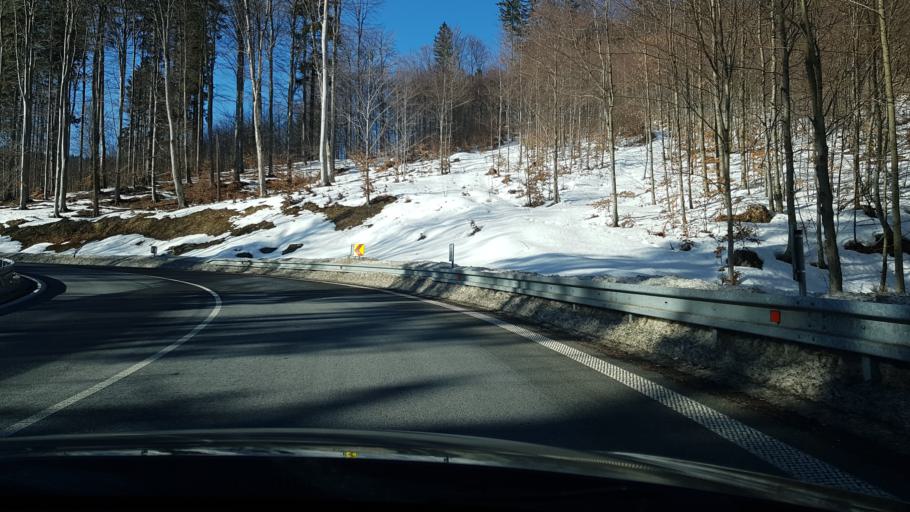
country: CZ
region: Olomoucky
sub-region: Okres Sumperk
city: Loucna nad Desnou
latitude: 50.1094
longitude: 17.1442
